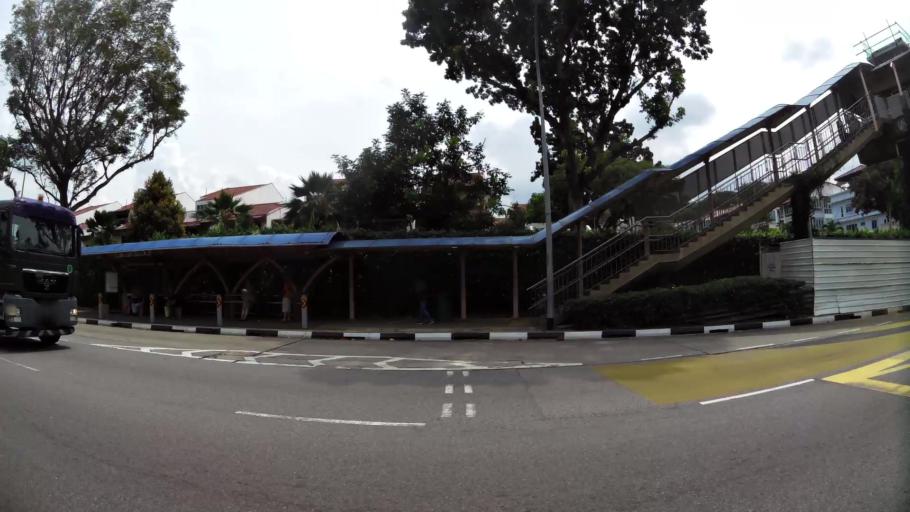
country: MY
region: Johor
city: Johor Bahru
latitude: 1.3781
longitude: 103.7576
